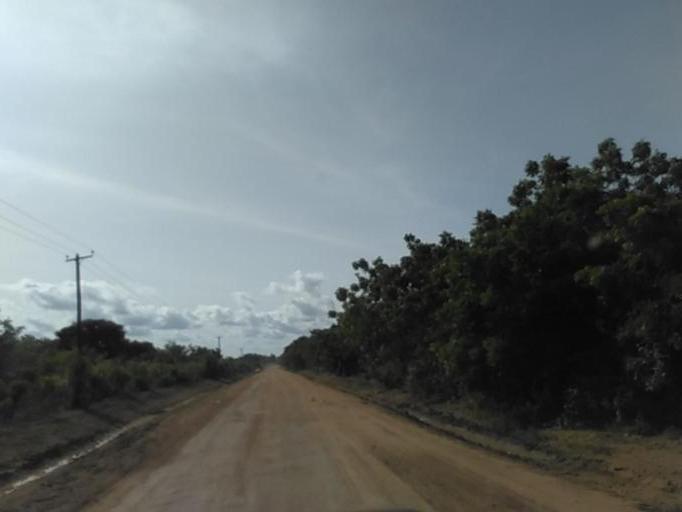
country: GH
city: Akropong
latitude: 6.0546
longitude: 0.2935
